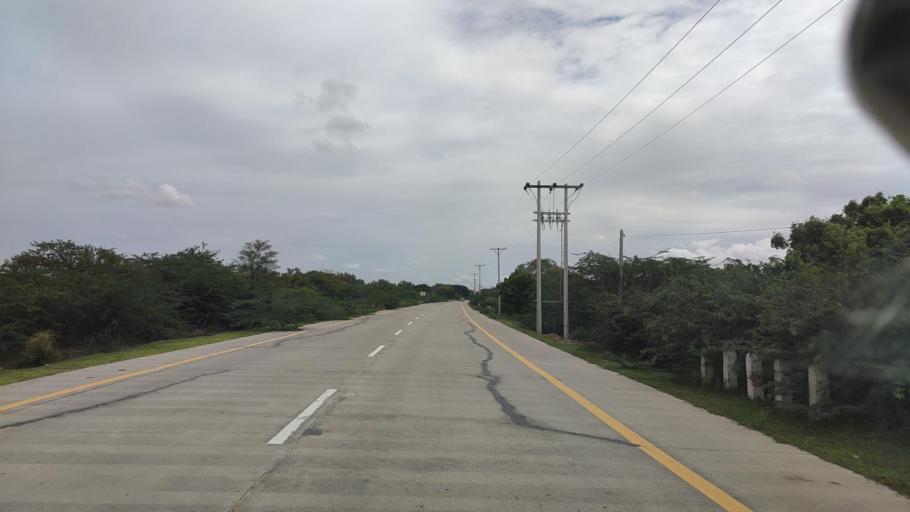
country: MM
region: Mandalay
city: Meiktila
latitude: 21.1278
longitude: 96.0280
